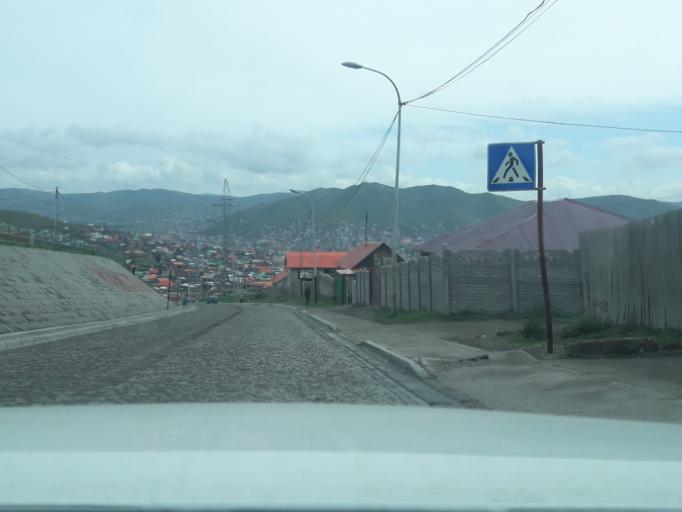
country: MN
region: Ulaanbaatar
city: Ulaanbaatar
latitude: 47.9674
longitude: 106.9019
